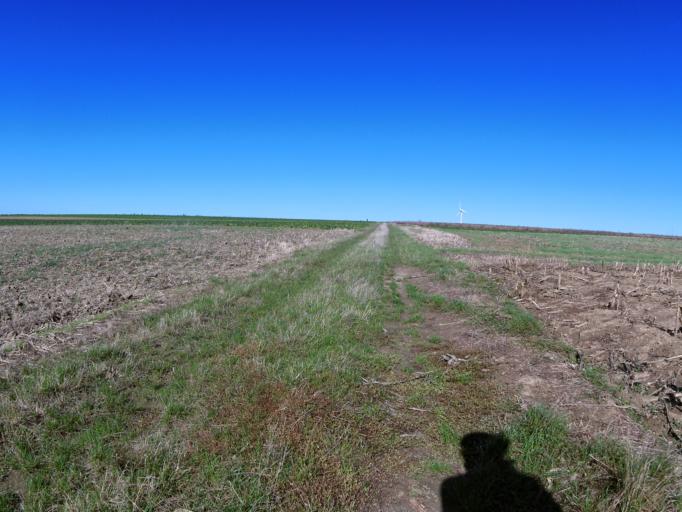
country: DE
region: Bavaria
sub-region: Regierungsbezirk Unterfranken
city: Theilheim
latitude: 49.7355
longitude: 10.0475
